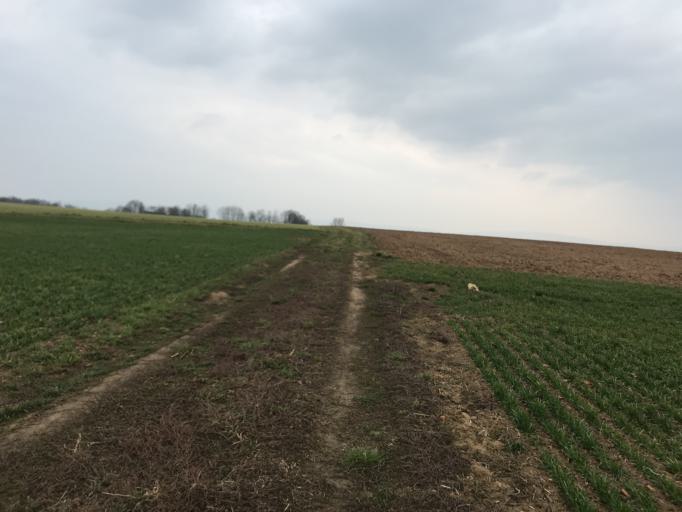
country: DE
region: Rheinland-Pfalz
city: Essenheim
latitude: 49.9538
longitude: 8.1396
